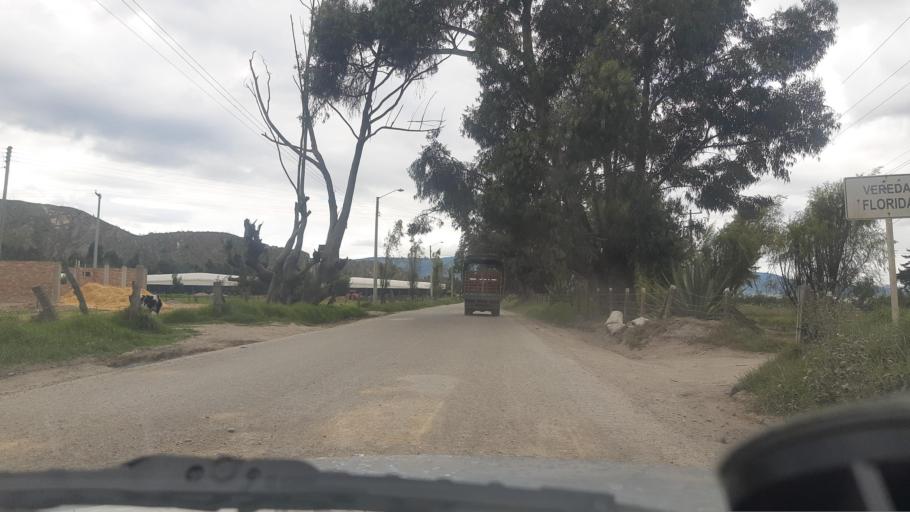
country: CO
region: Cundinamarca
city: Cucunuba
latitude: 5.2565
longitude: -73.7844
